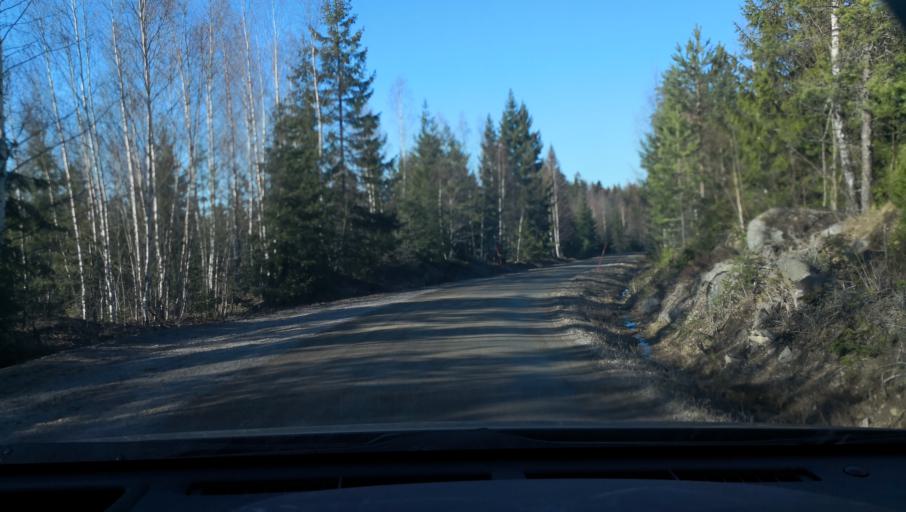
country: SE
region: Vaestmanland
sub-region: Sala Kommun
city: Sala
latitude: 60.1612
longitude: 16.6283
